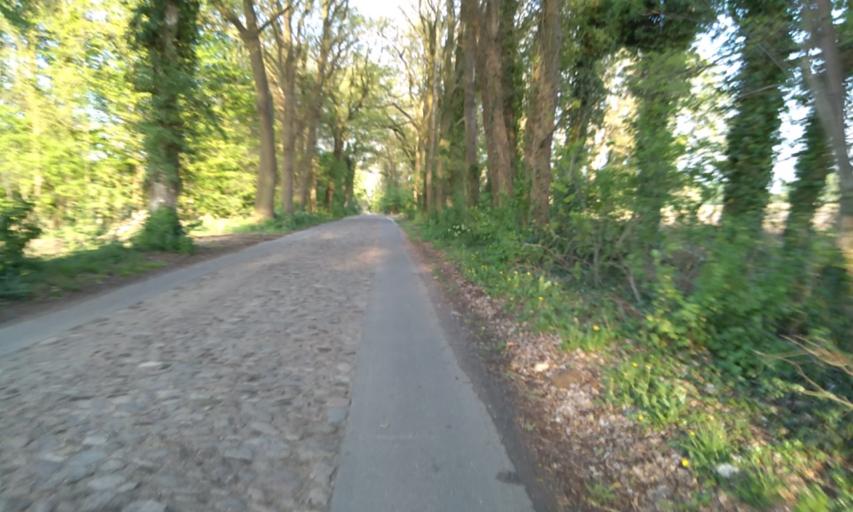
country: DE
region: Lower Saxony
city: Dollern
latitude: 53.5329
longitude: 9.5550
